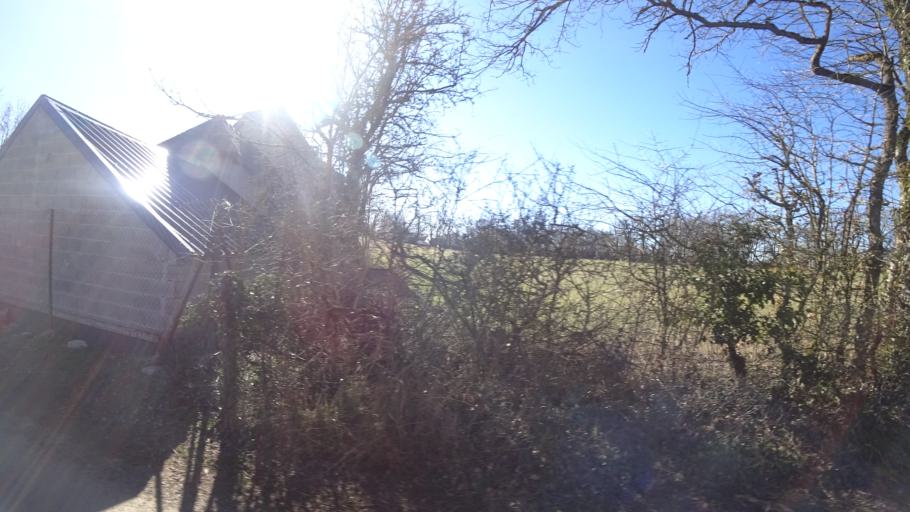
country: FR
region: Midi-Pyrenees
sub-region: Departement de l'Aveyron
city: Sebazac-Concoures
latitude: 44.4079
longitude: 2.5626
